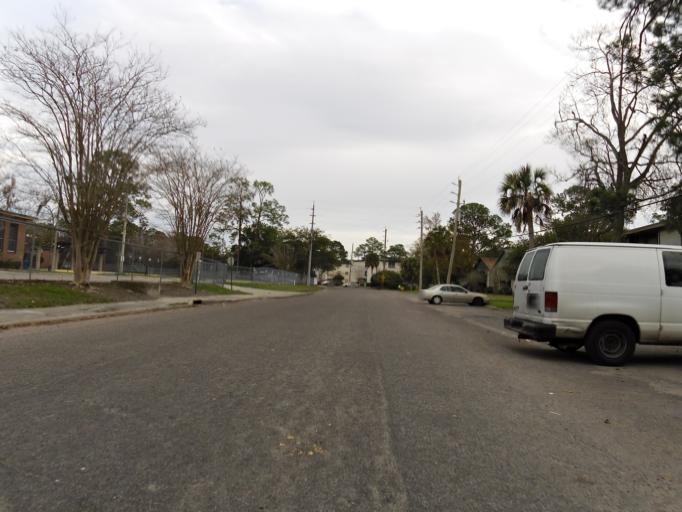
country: US
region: Florida
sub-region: Duval County
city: Jacksonville
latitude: 30.2496
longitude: -81.6330
